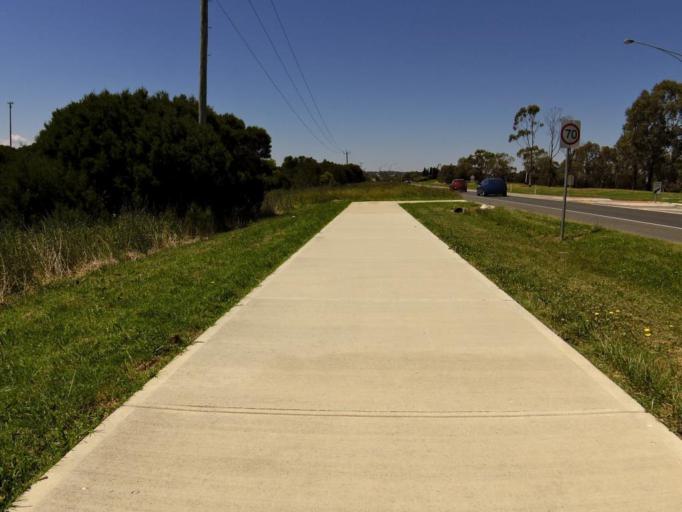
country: AU
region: Victoria
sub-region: Casey
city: Narre Warren South
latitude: -38.0578
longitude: 145.3218
